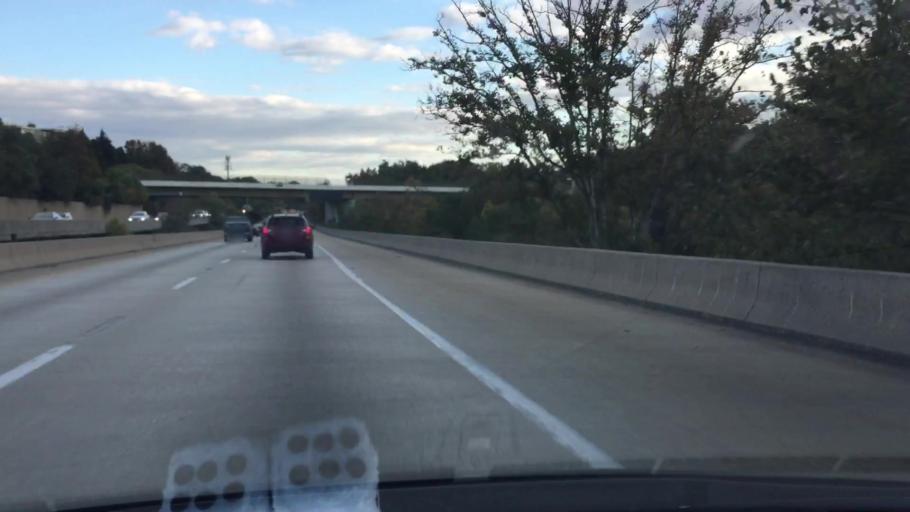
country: US
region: Pennsylvania
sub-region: Delaware County
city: Swarthmore
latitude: 39.8890
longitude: -75.3573
